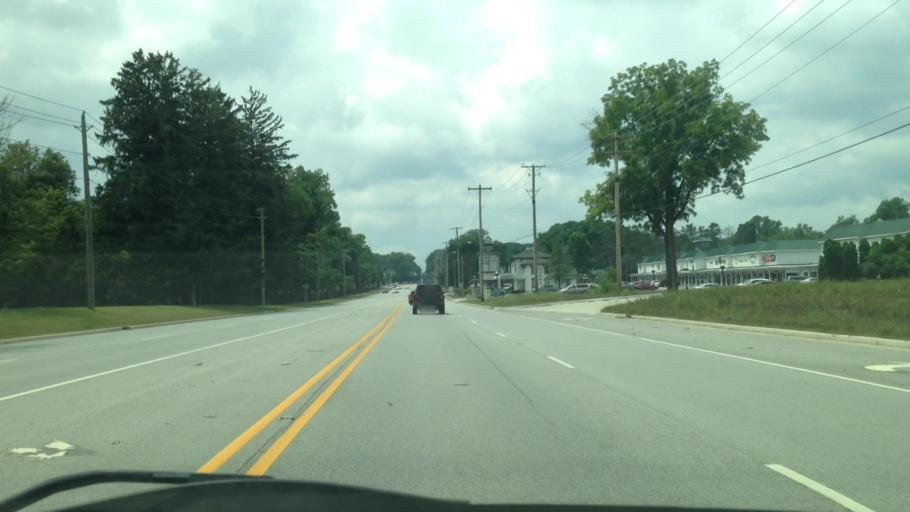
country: US
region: Indiana
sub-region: Saint Joseph County
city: Georgetown
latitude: 41.7240
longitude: -86.1819
